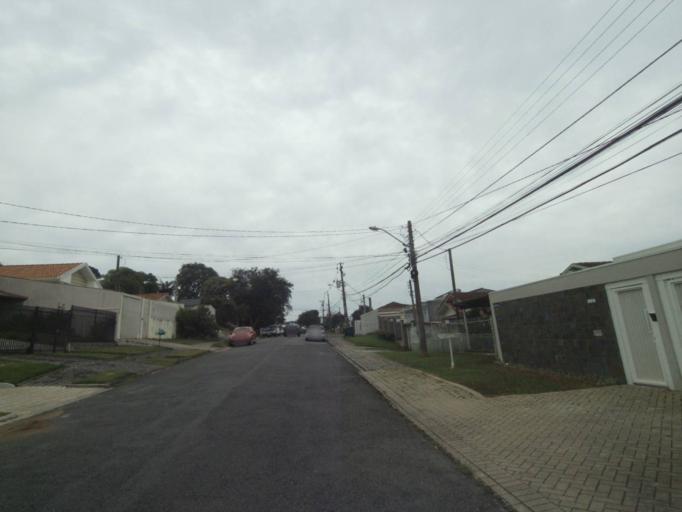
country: BR
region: Parana
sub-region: Curitiba
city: Curitiba
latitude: -25.3976
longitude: -49.2650
